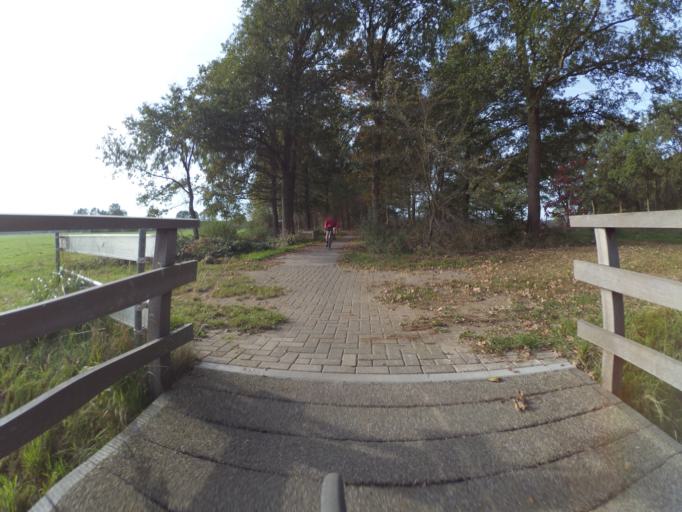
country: NL
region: Overijssel
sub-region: Gemeente Deventer
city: Schalkhaar
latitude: 52.3020
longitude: 6.2513
